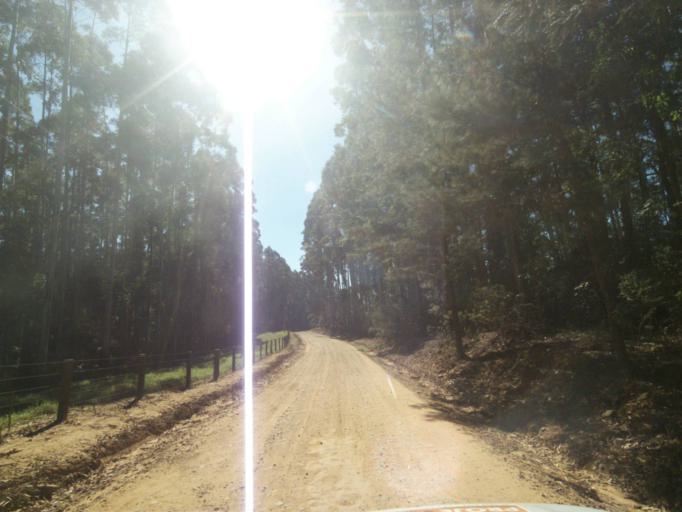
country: BR
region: Parana
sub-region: Tibagi
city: Tibagi
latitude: -24.5547
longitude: -50.6213
